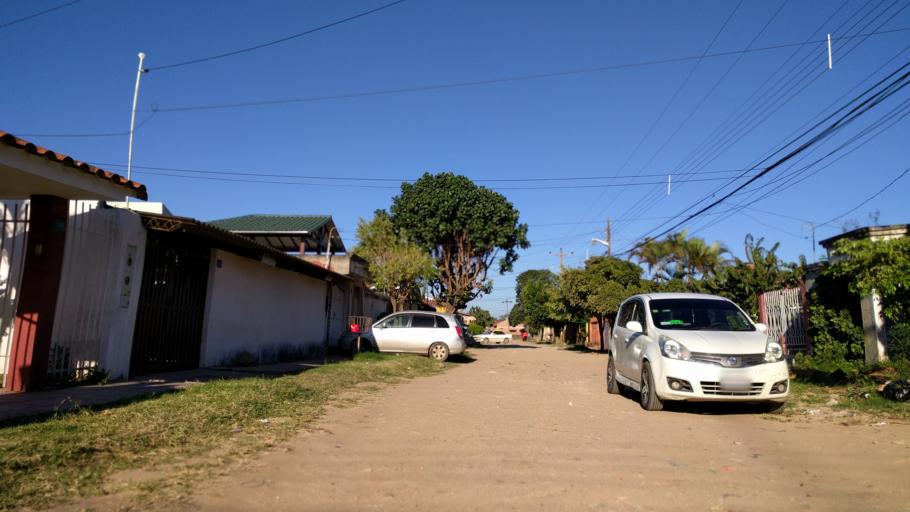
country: BO
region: Santa Cruz
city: Santa Cruz de la Sierra
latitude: -17.8100
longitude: -63.2246
